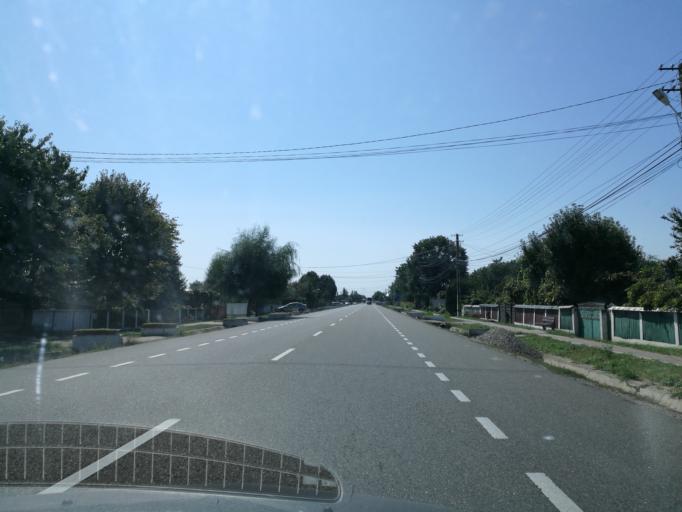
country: RO
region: Bacau
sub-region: Comuna Filipesti
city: Filipesti
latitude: 46.7486
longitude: 26.8841
